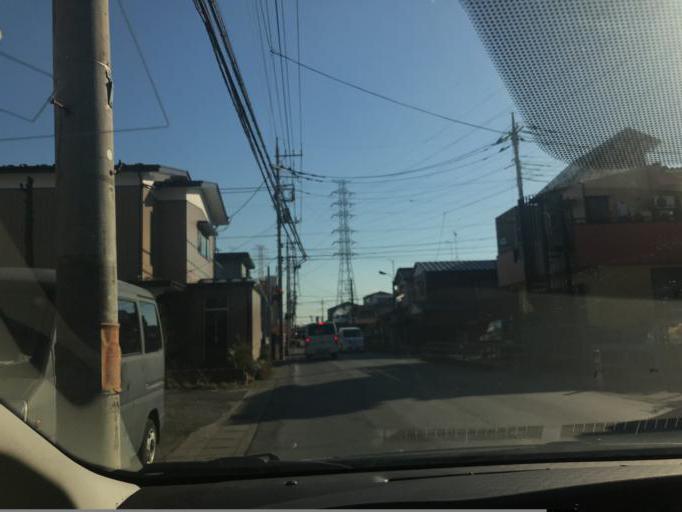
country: JP
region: Saitama
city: Yashio-shi
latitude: 35.8352
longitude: 139.8361
